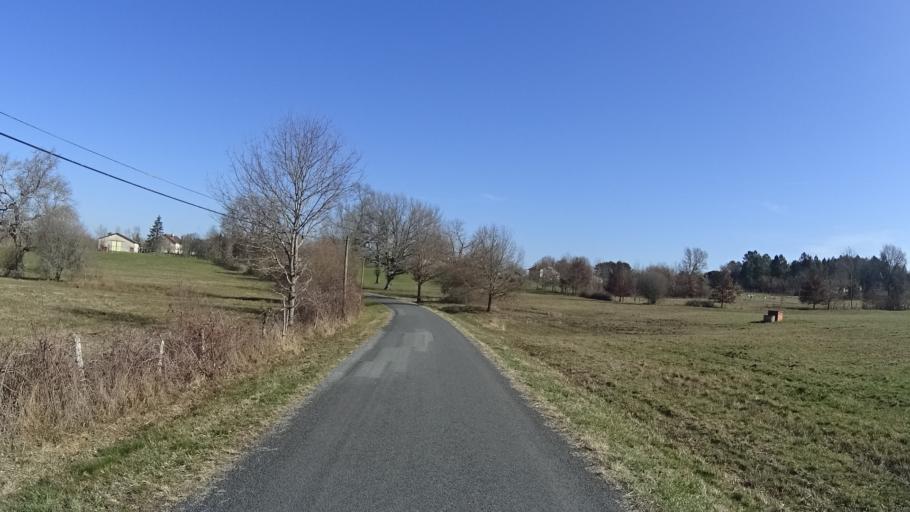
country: FR
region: Aquitaine
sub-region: Departement de la Dordogne
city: Montpon-Menesterol
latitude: 45.1101
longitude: 0.2112
